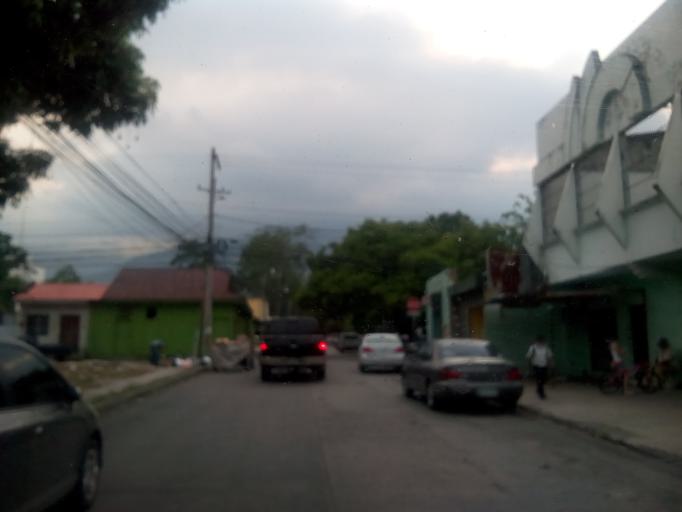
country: HN
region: Cortes
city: San Pedro Sula
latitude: 15.5092
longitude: -88.0252
